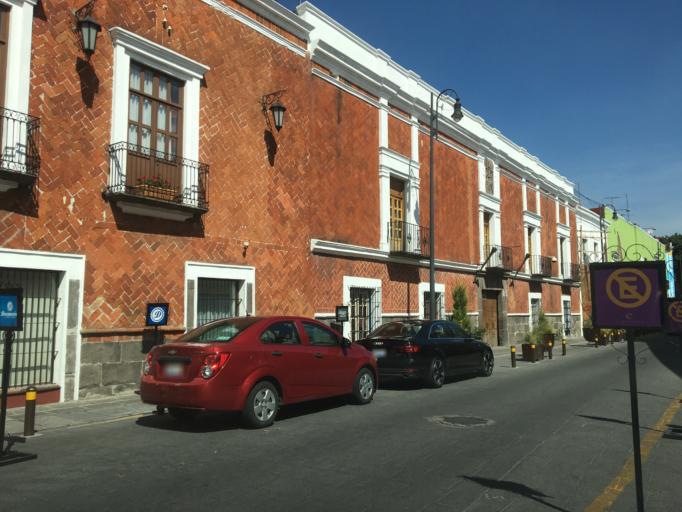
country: MX
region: Puebla
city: Puebla
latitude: 19.0409
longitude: -98.1942
